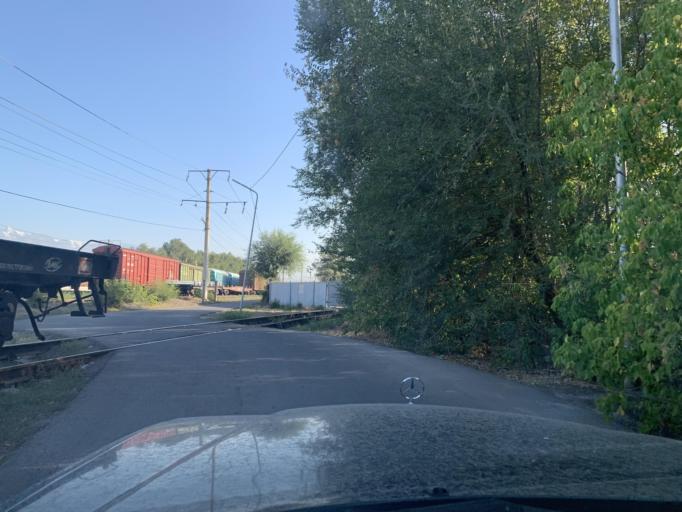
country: KZ
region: Almaty Oblysy
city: Energeticheskiy
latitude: 43.3887
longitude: 76.9988
